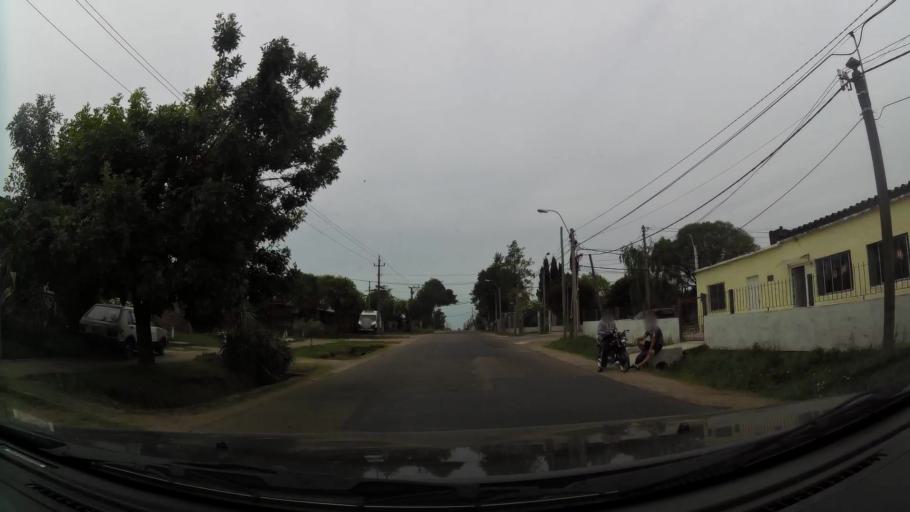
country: UY
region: Canelones
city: Las Piedras
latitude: -34.7430
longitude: -56.2277
